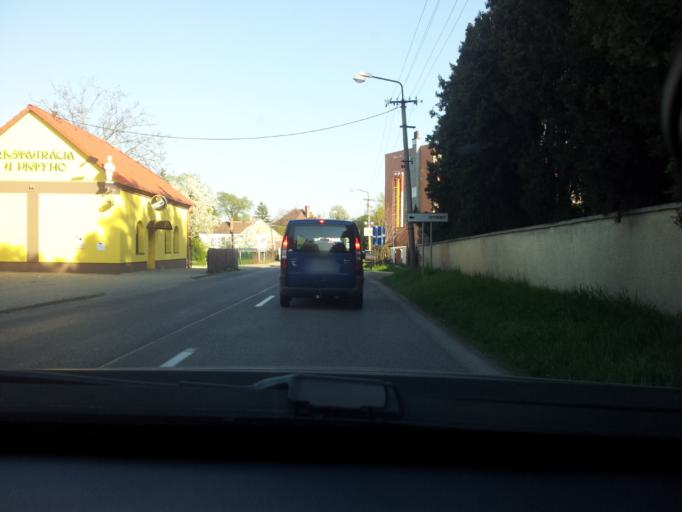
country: SK
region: Nitriansky
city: Zlate Moravce
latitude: 48.3804
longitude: 18.3982
